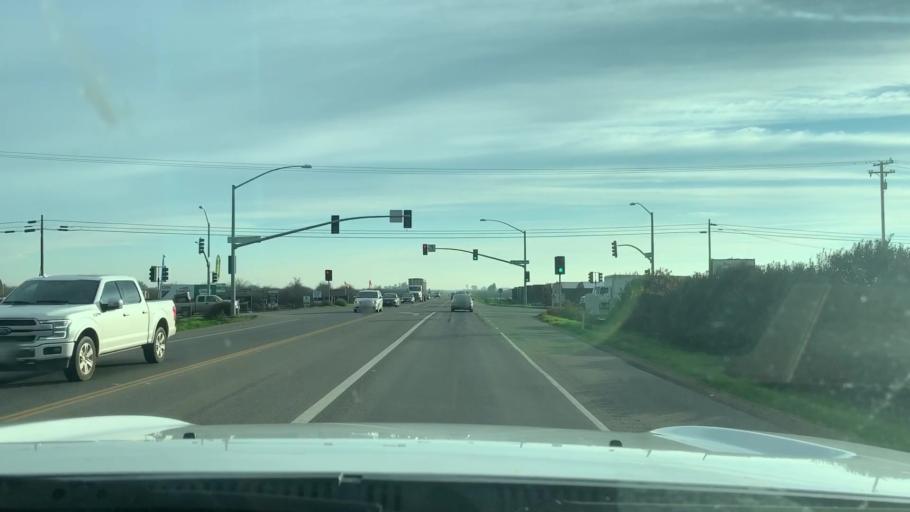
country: US
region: California
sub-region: Fresno County
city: Riverdale
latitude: 36.4317
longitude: -119.8011
